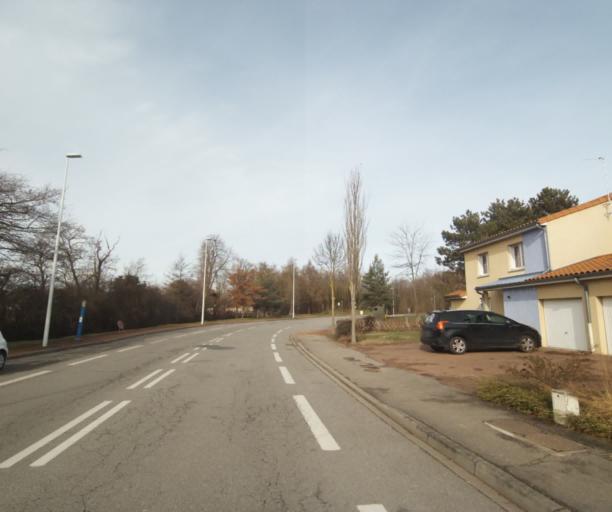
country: FR
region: Rhone-Alpes
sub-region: Departement de la Loire
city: Riorges
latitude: 46.0268
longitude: 4.0483
